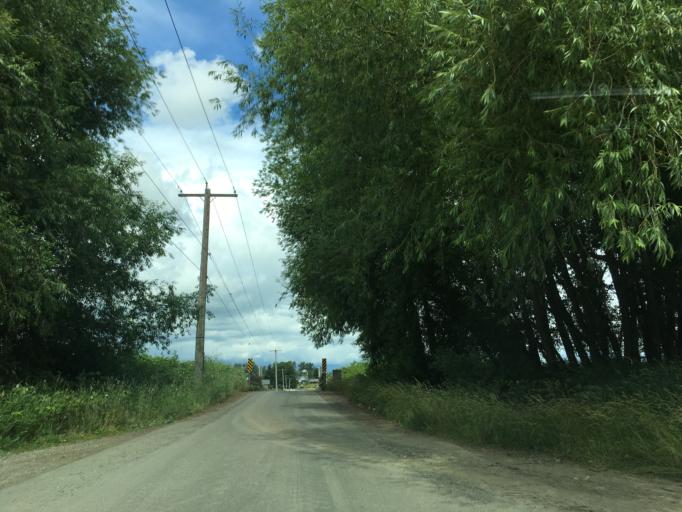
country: US
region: Washington
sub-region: Whatcom County
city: Lynden
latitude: 48.9259
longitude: -122.4964
